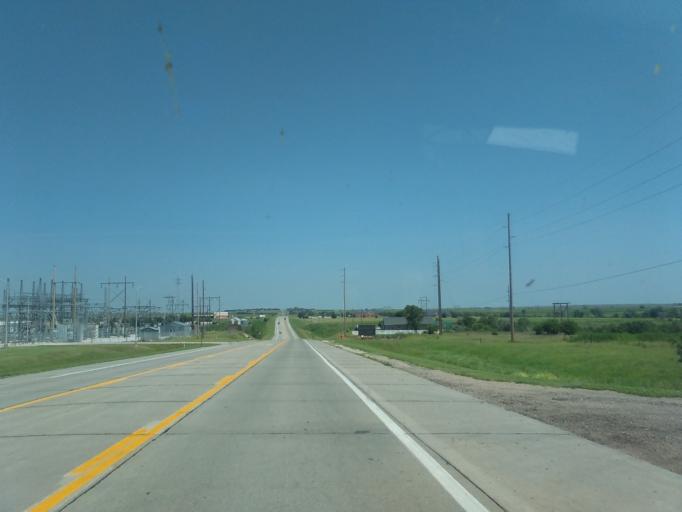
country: US
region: Nebraska
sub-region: Red Willow County
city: McCook
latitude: 40.2198
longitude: -100.6500
